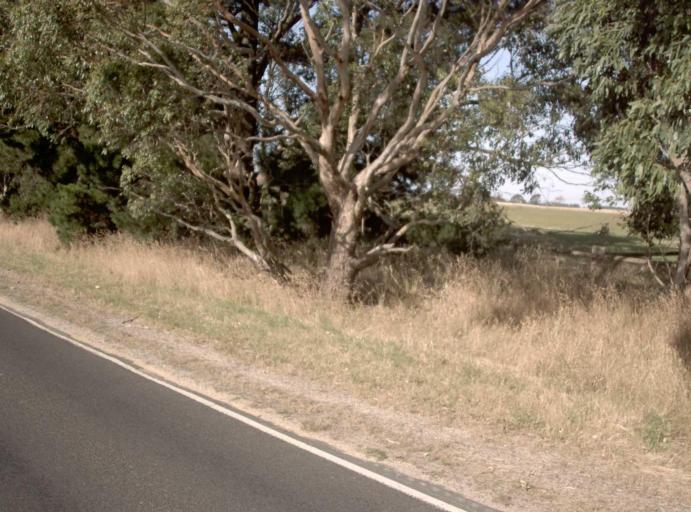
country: AU
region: Victoria
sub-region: Latrobe
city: Traralgon
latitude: -38.2254
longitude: 146.5206
